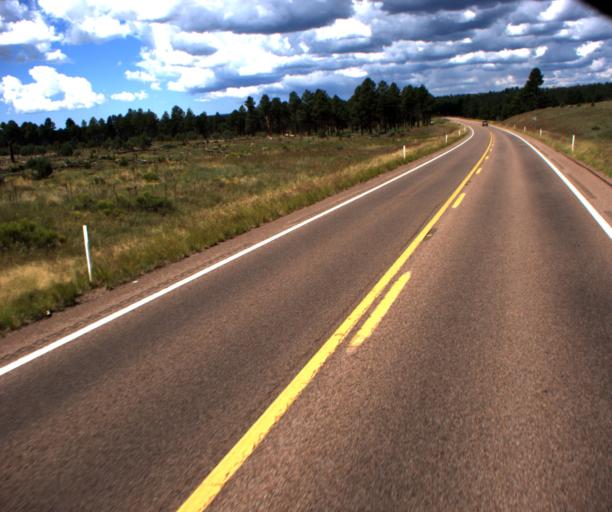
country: US
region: Arizona
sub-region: Navajo County
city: Heber-Overgaard
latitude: 34.3925
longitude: -110.5120
